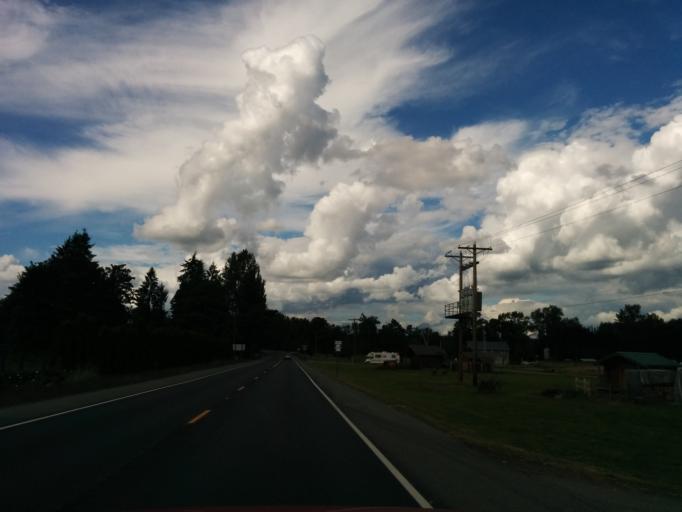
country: US
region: Washington
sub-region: Snohomish County
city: Monroe
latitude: 47.8399
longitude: -121.9693
